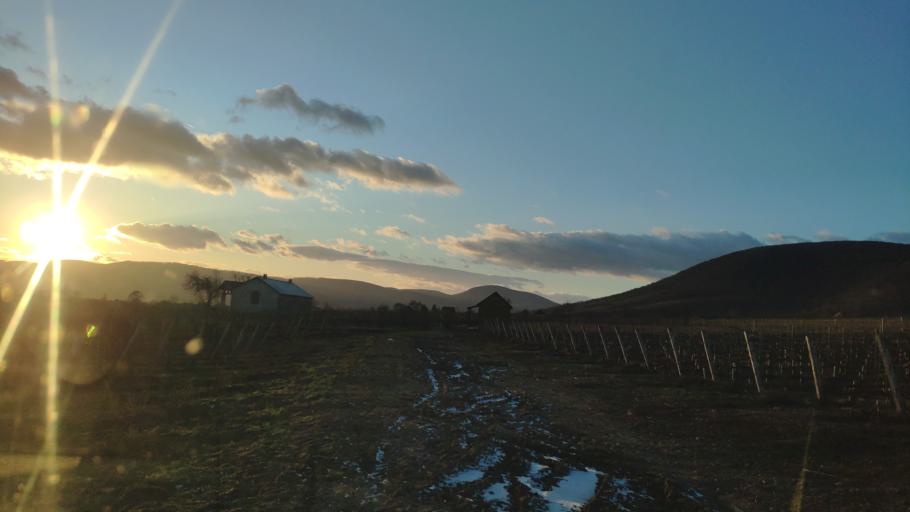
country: HU
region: Borsod-Abauj-Zemplen
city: Olaszliszka
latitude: 48.2745
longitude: 21.4075
